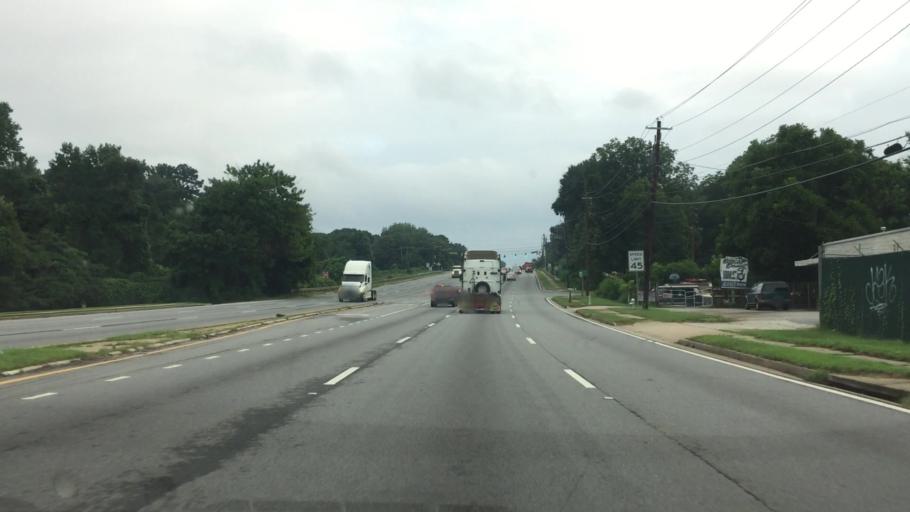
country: US
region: Georgia
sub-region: DeKalb County
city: Gresham Park
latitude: 33.6893
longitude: -84.3492
